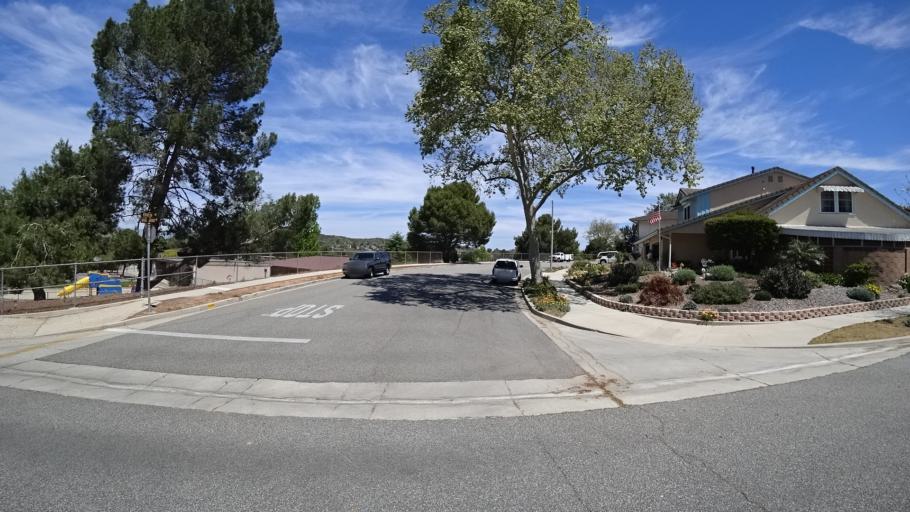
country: US
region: California
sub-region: Ventura County
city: Casa Conejo
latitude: 34.1572
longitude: -118.9534
